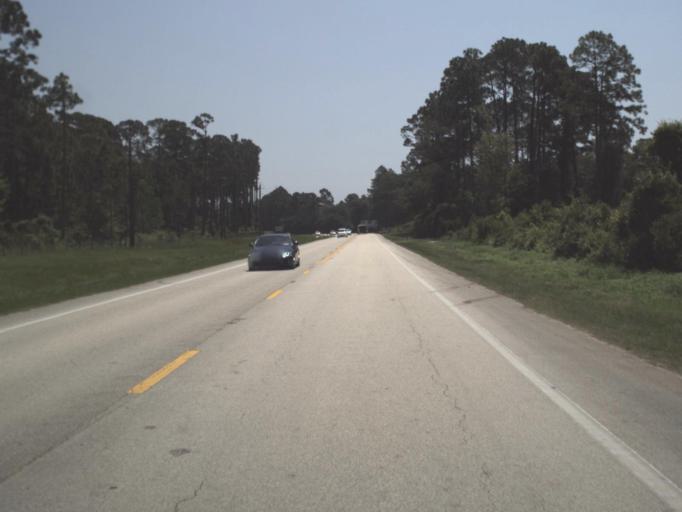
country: US
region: Florida
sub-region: Saint Johns County
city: Butler Beach
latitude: 29.7570
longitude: -81.2781
